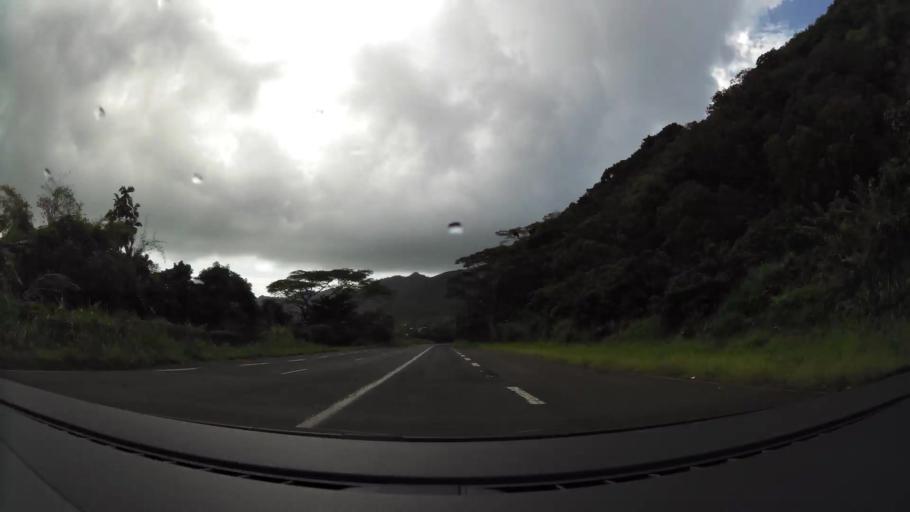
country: GP
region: Guadeloupe
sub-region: Guadeloupe
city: Gourbeyre
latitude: 15.9981
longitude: -61.6773
